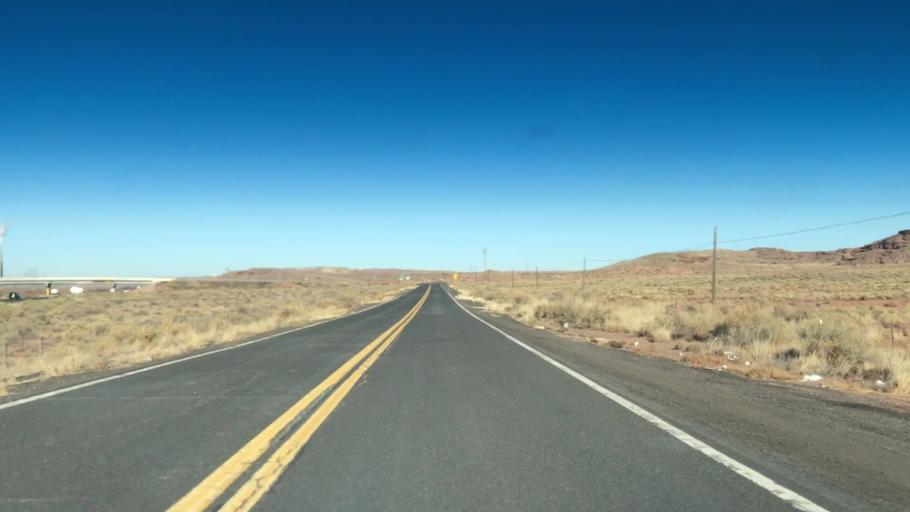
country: US
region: Arizona
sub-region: Navajo County
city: Joseph City
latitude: 34.9209
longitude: -110.2569
